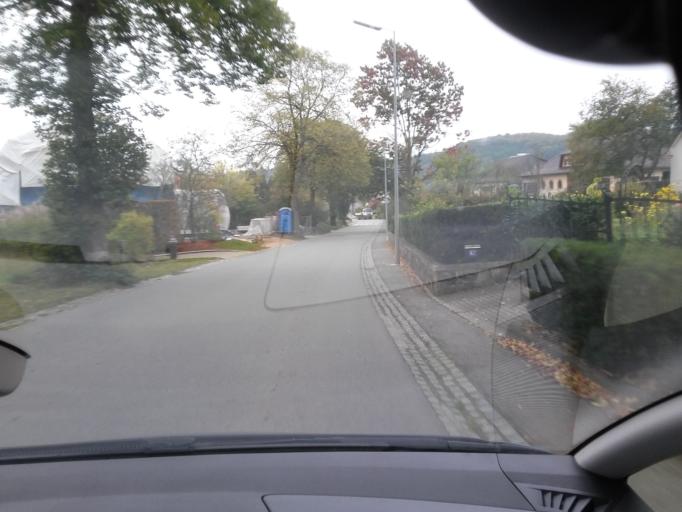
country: LU
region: Diekirch
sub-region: Canton de Redange
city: Beckerich
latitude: 49.7245
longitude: 5.9014
